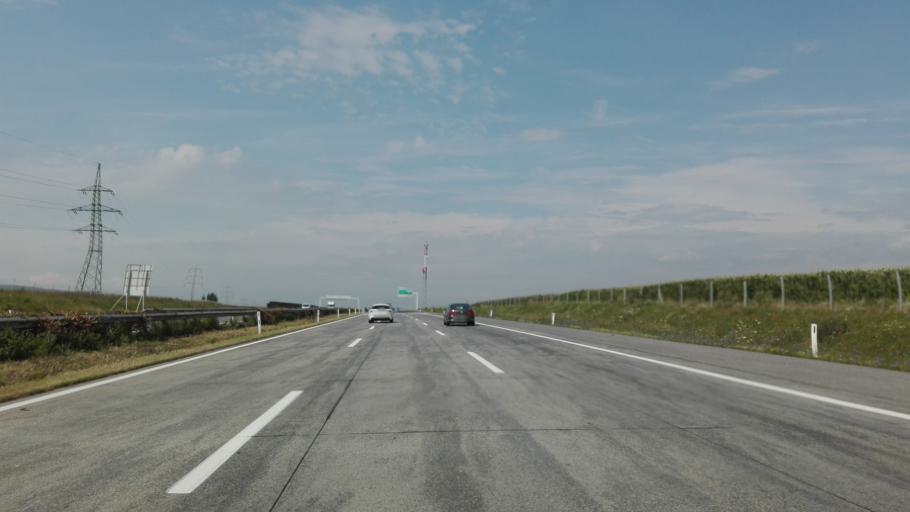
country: AT
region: Lower Austria
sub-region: Sankt Polten Stadt
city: Sankt Poelten
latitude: 48.1779
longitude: 15.5955
